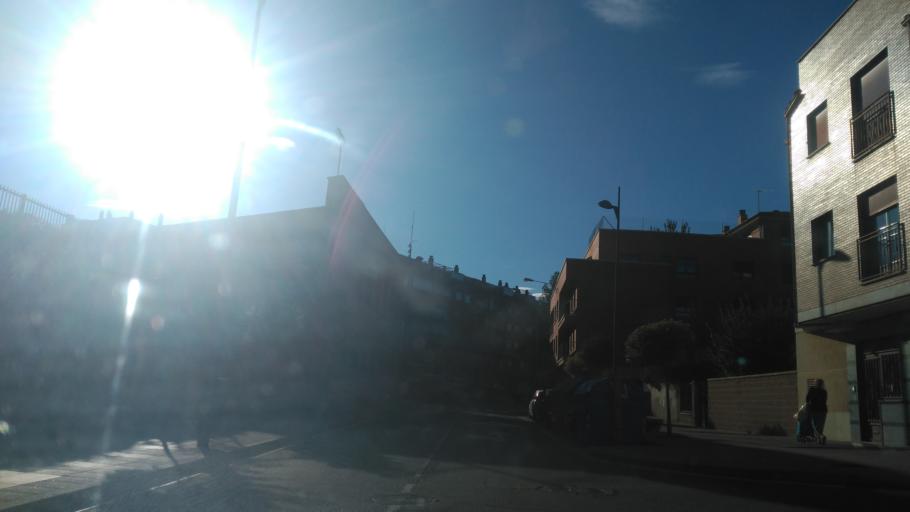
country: ES
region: Castille and Leon
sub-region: Provincia de Salamanca
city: Salamanca
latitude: 40.9755
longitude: -5.6714
